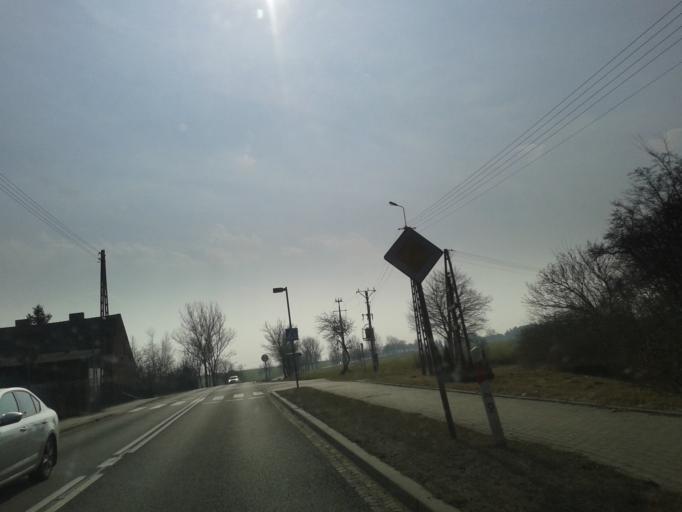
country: PL
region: Pomeranian Voivodeship
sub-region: Powiat czluchowski
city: Debrzno
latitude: 53.5955
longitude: 17.1295
